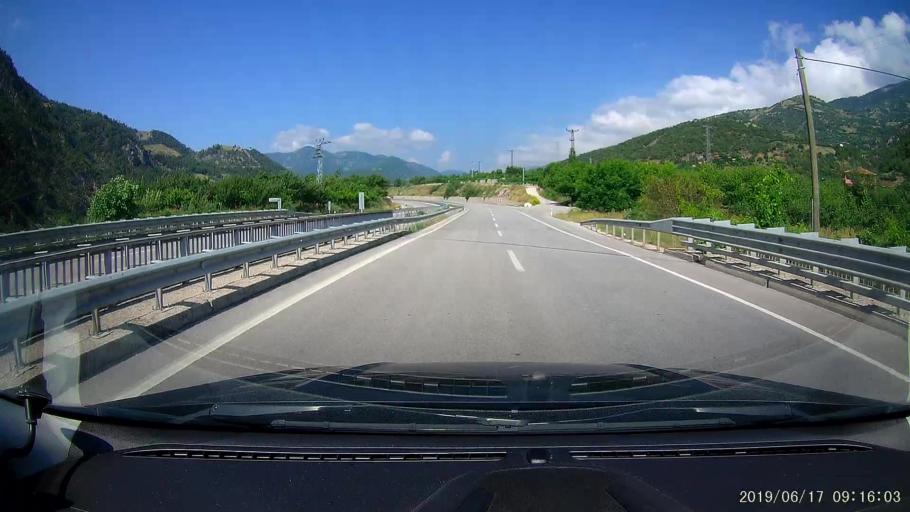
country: TR
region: Amasya
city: Akdag
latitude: 40.7463
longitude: 36.0215
